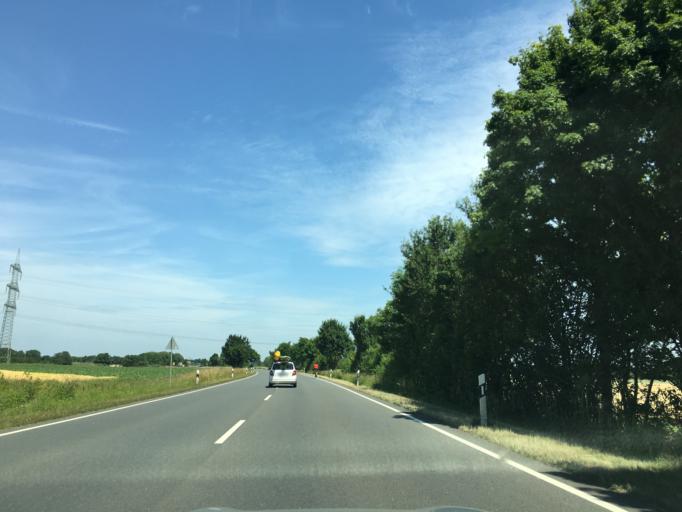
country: DE
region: Hesse
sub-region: Regierungsbezirk Darmstadt
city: Riedstadt
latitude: 49.8601
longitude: 8.4859
